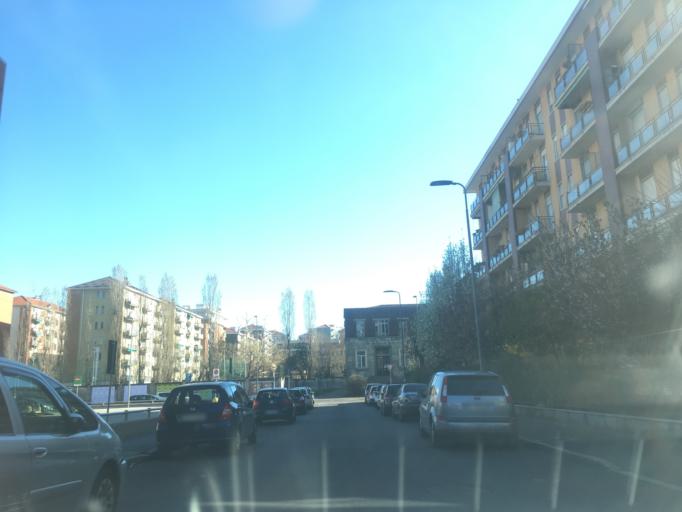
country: IT
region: Lombardy
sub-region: Citta metropolitana di Milano
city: Romano Banco
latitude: 45.4637
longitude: 9.1321
